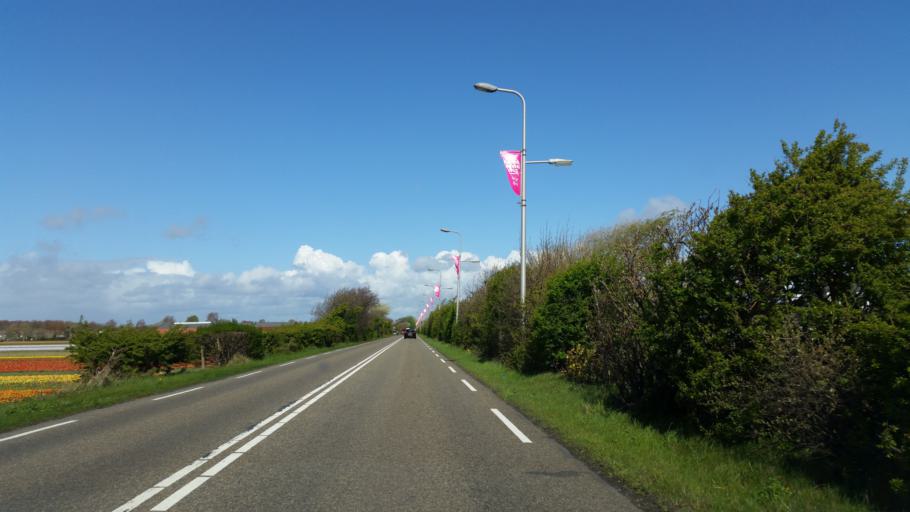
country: NL
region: South Holland
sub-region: Gemeente Noordwijkerhout
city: Noordwijkerhout
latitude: 52.2543
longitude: 4.4799
